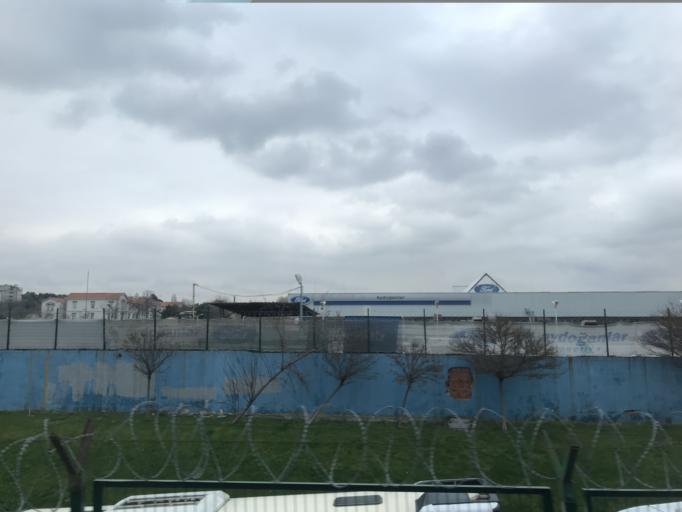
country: TR
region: Istanbul
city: Zeytinburnu
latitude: 40.9928
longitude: 28.9176
